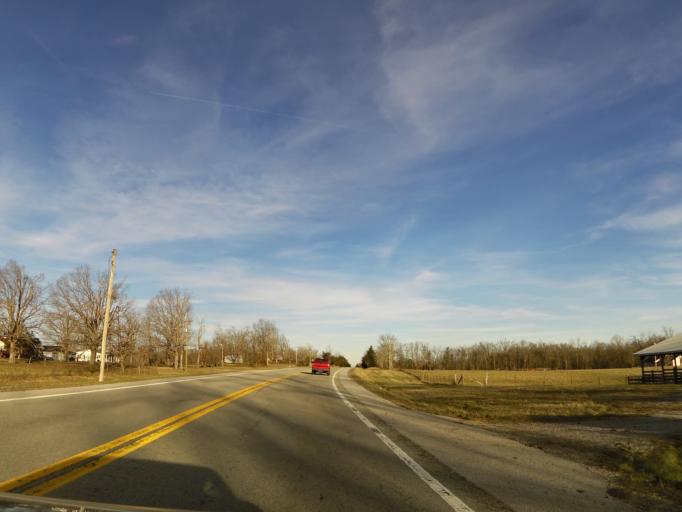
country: US
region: Tennessee
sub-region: Putnam County
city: Monterey
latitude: 35.9713
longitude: -85.2175
